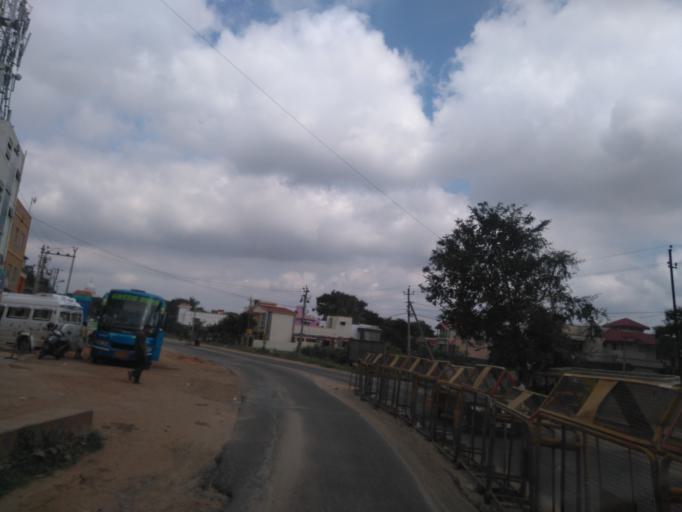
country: IN
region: Karnataka
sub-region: Mysore
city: Mysore
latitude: 12.2990
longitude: 76.6981
